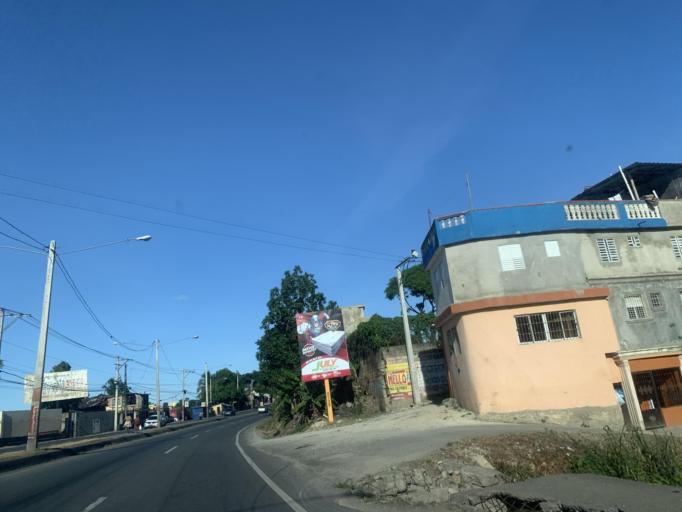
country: DO
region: San Cristobal
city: El Carril
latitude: 18.4359
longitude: -70.0153
